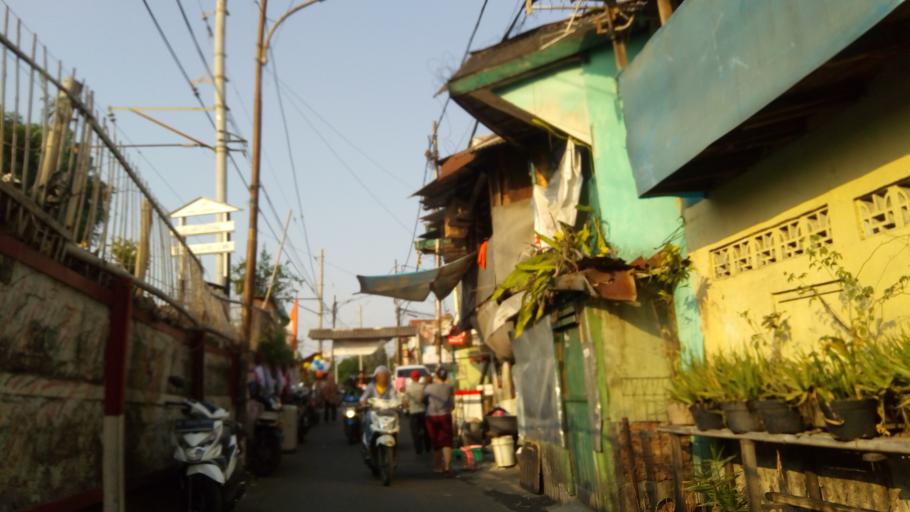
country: ID
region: Jakarta Raya
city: Jakarta
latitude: -6.2063
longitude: 106.8432
